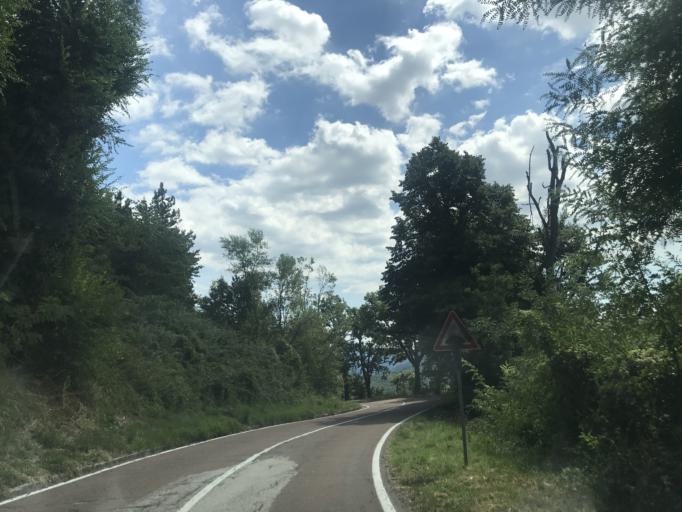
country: IT
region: Emilia-Romagna
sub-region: Provincia di Bologna
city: Grizzana
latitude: 44.2581
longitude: 11.1584
